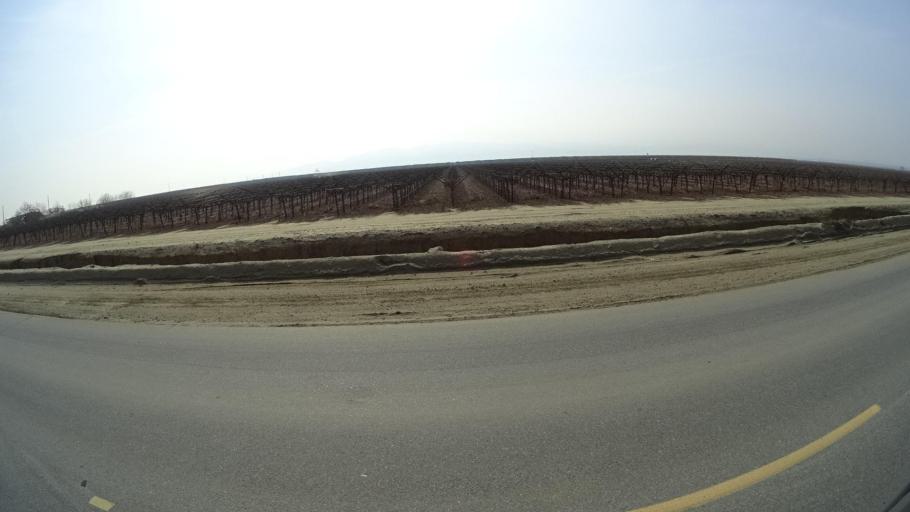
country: US
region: California
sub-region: Kern County
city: Weedpatch
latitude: 35.0953
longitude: -119.0139
